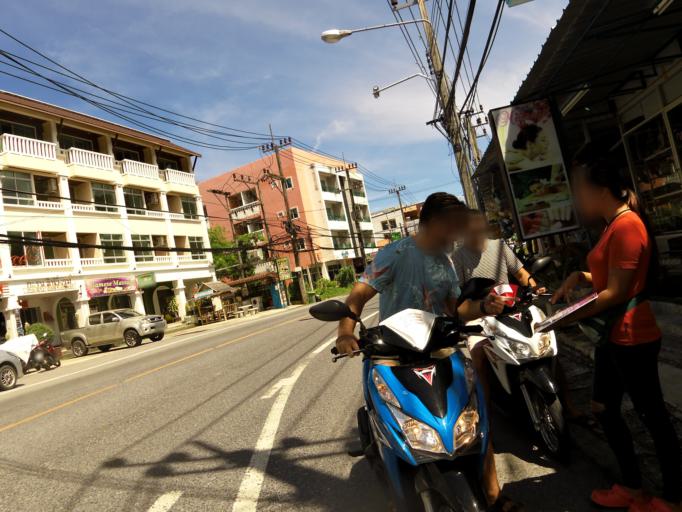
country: TH
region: Phuket
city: Ban Karon
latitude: 7.8450
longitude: 98.2992
